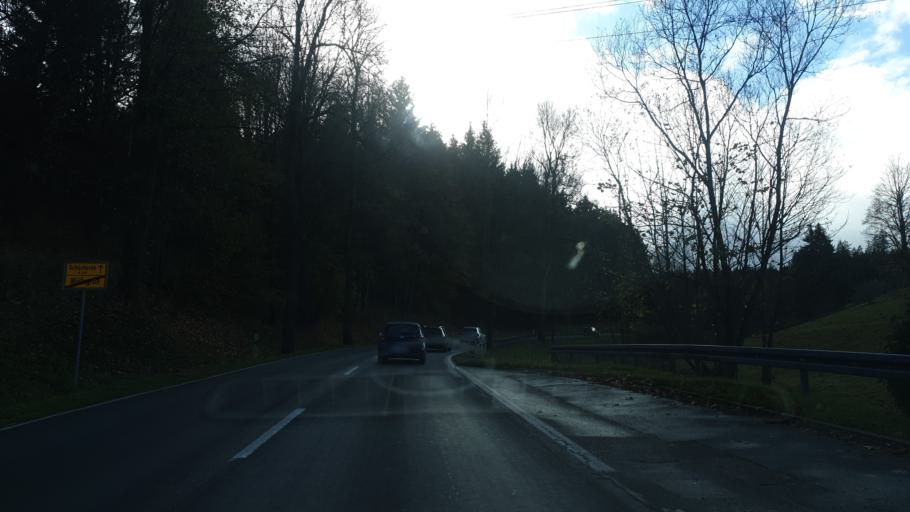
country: DE
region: Saxony
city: Eibenstock
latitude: 50.5175
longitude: 12.6130
